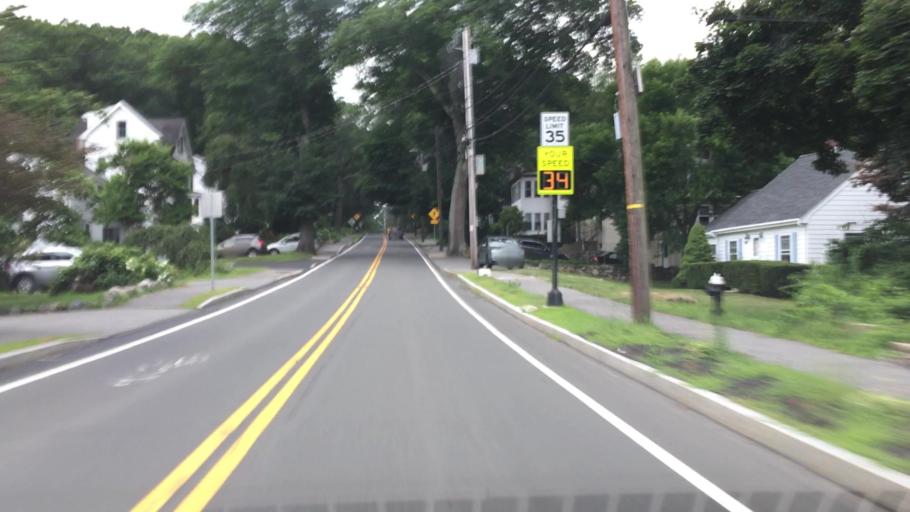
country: US
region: Massachusetts
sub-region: Middlesex County
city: Lexington
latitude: 42.4330
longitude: -71.2428
